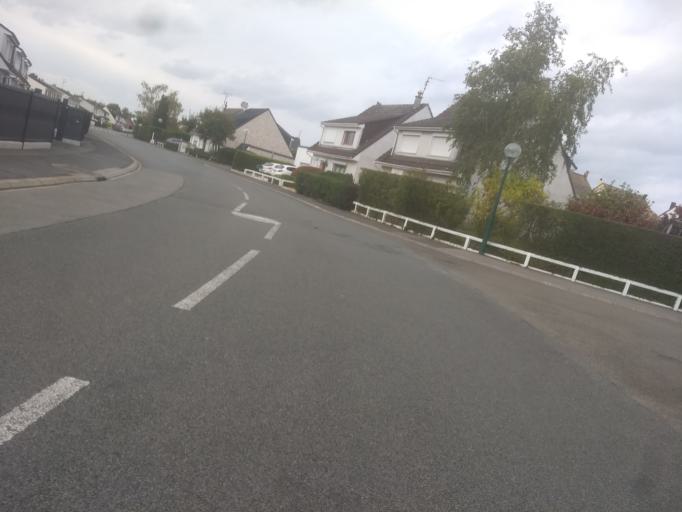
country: FR
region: Nord-Pas-de-Calais
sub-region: Departement du Pas-de-Calais
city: Agny
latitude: 50.2672
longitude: 2.7727
